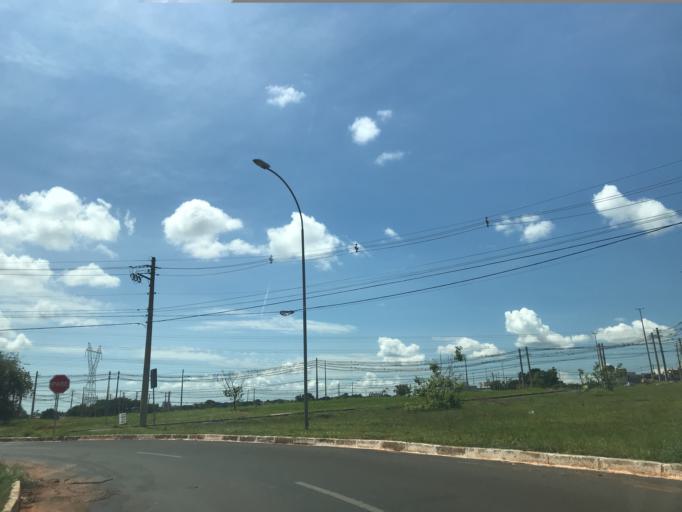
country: BR
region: Federal District
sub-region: Brasilia
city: Brasilia
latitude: -15.8471
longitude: -48.0332
